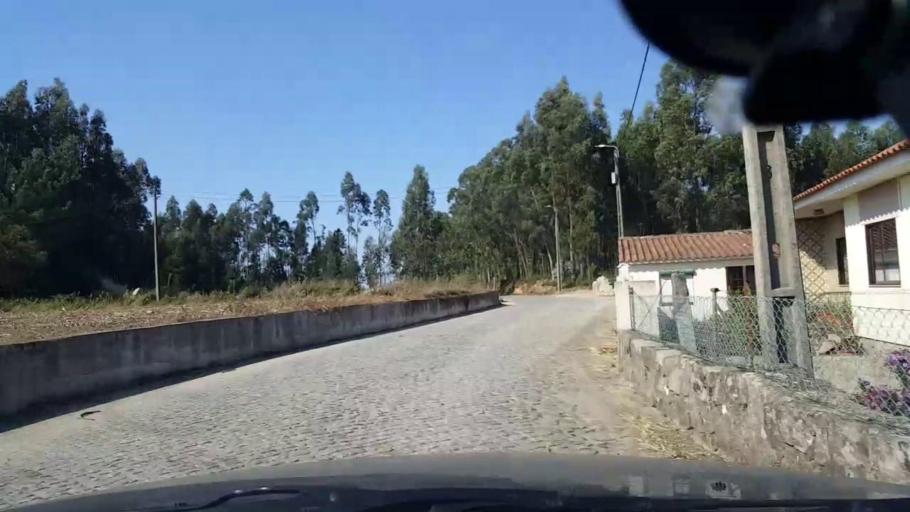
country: PT
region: Porto
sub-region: Vila do Conde
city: Arvore
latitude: 41.3591
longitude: -8.6950
